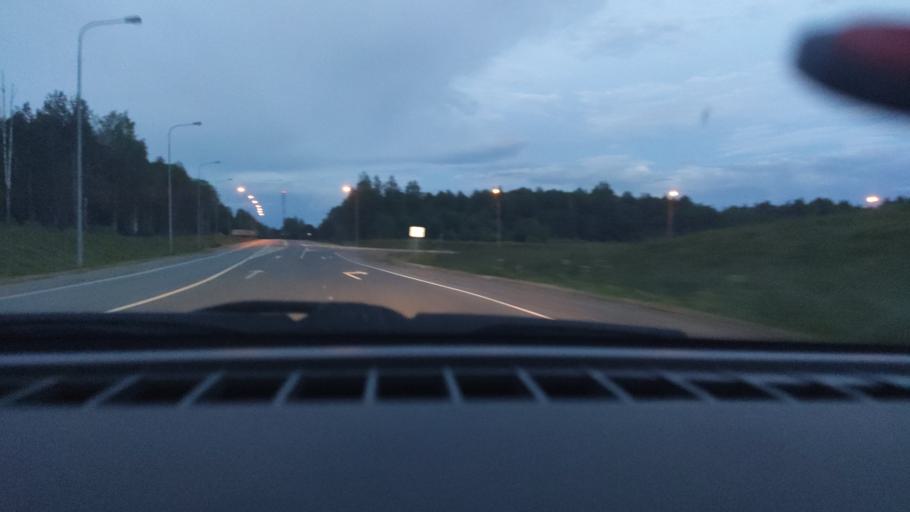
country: RU
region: Perm
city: Bershet'
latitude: 57.7359
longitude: 56.3470
